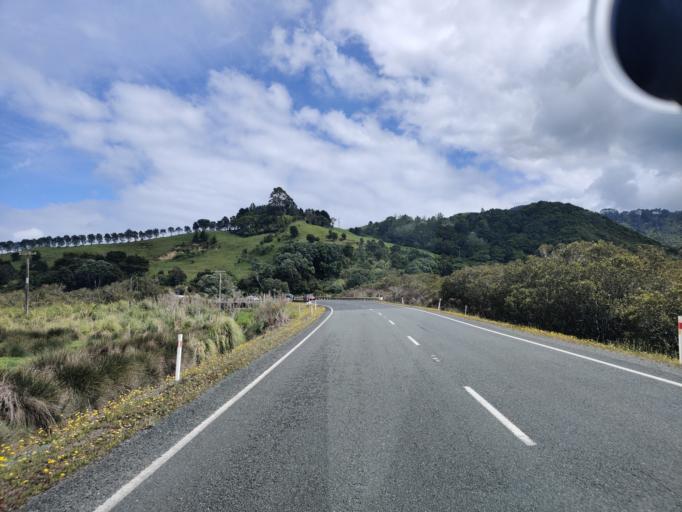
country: NZ
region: Northland
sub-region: Far North District
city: Taipa
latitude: -35.0565
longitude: 173.7018
